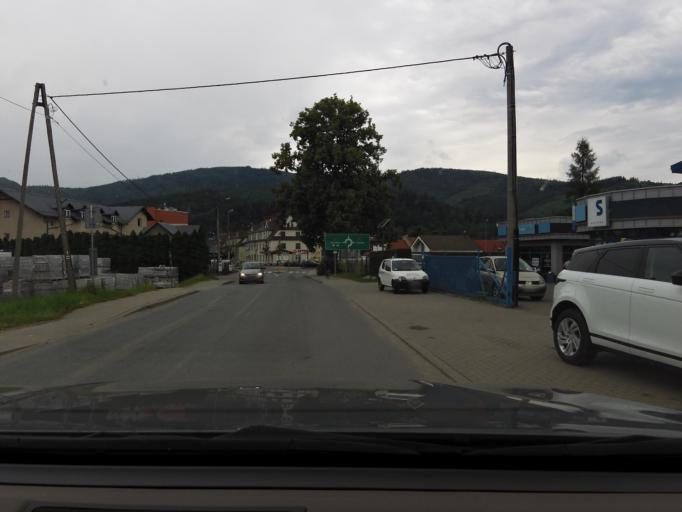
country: PL
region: Silesian Voivodeship
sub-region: Powiat zywiecki
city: Wegierska Gorka
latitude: 49.6025
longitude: 19.1151
